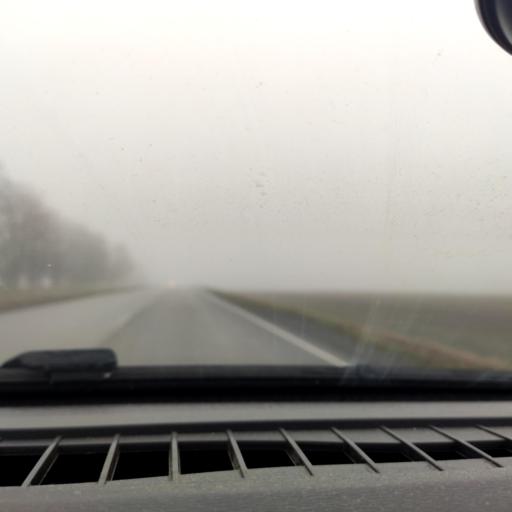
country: RU
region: Belgorod
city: Ilovka
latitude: 50.7645
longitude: 38.7459
